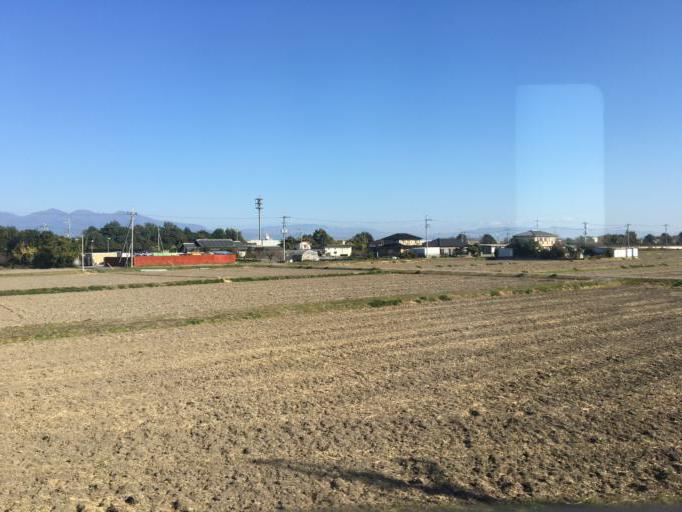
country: JP
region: Gunma
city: Isesaki
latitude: 36.3487
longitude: 139.1526
